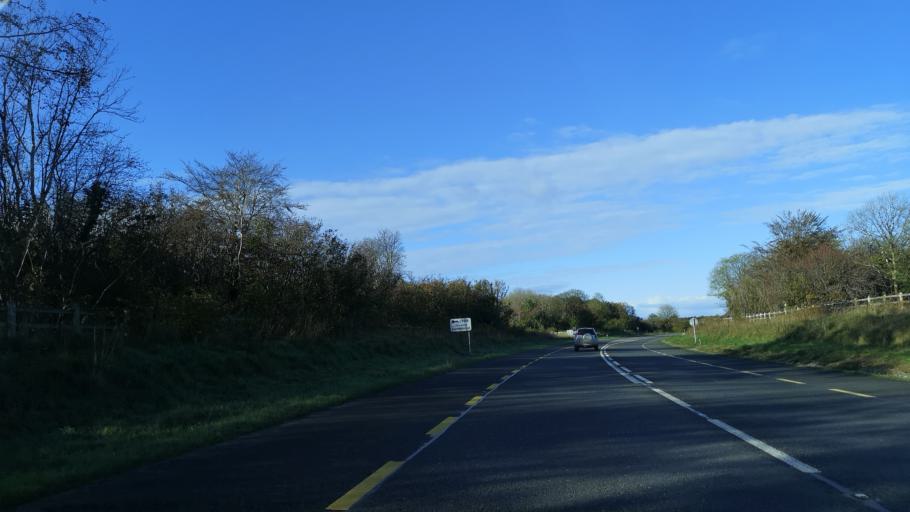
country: IE
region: Connaught
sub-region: County Galway
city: Claregalway
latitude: 53.4269
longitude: -9.0469
